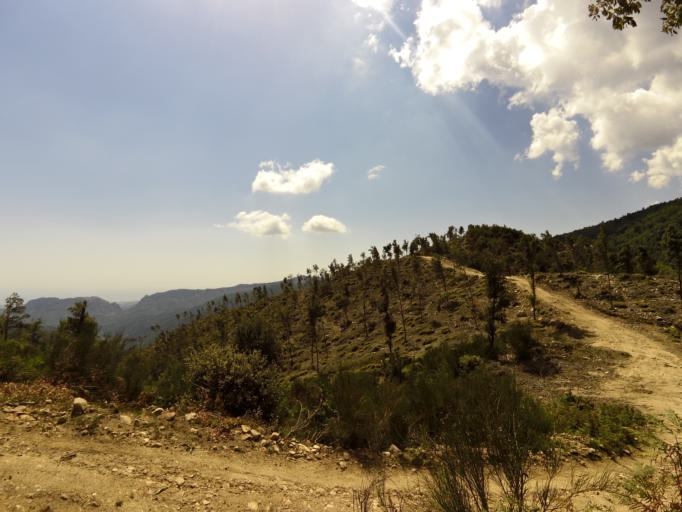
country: IT
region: Calabria
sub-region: Provincia di Vibo-Valentia
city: Nardodipace
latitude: 38.5068
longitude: 16.3905
